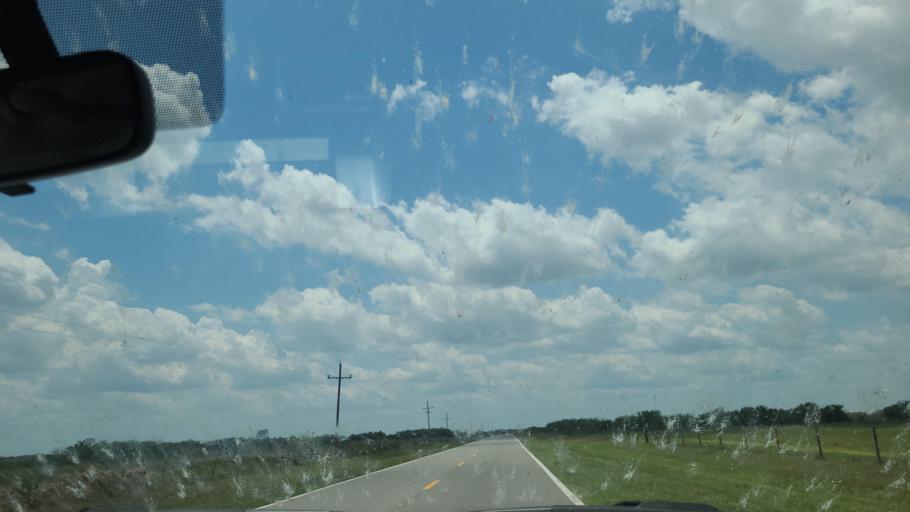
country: US
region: Florida
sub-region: Glades County
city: Buckhead Ridge
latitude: 27.2563
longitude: -81.0539
